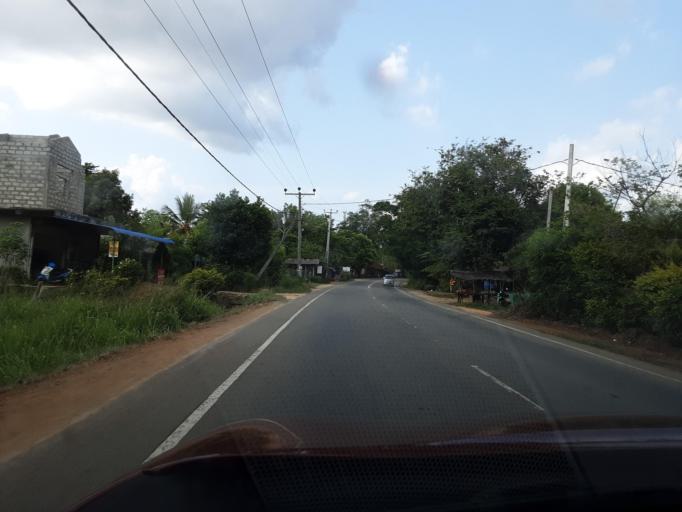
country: LK
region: Uva
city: Haputale
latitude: 6.5258
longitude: 81.1244
